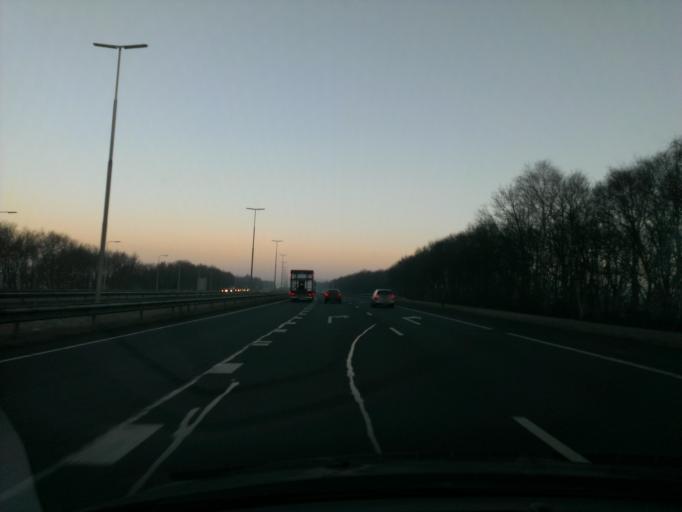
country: NL
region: Gelderland
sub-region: Gemeente Hattem
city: Hattem
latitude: 52.4800
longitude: 6.0327
